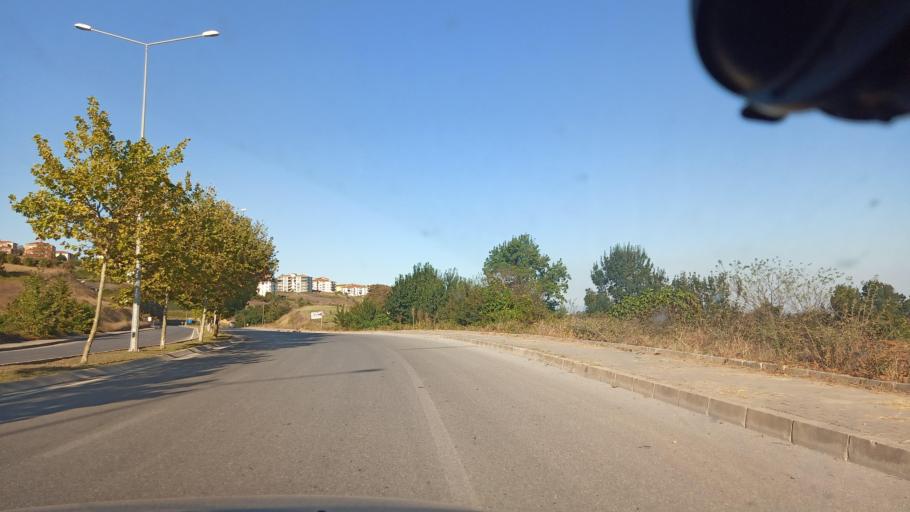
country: TR
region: Sakarya
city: Kazimpasa
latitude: 40.8519
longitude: 30.2862
